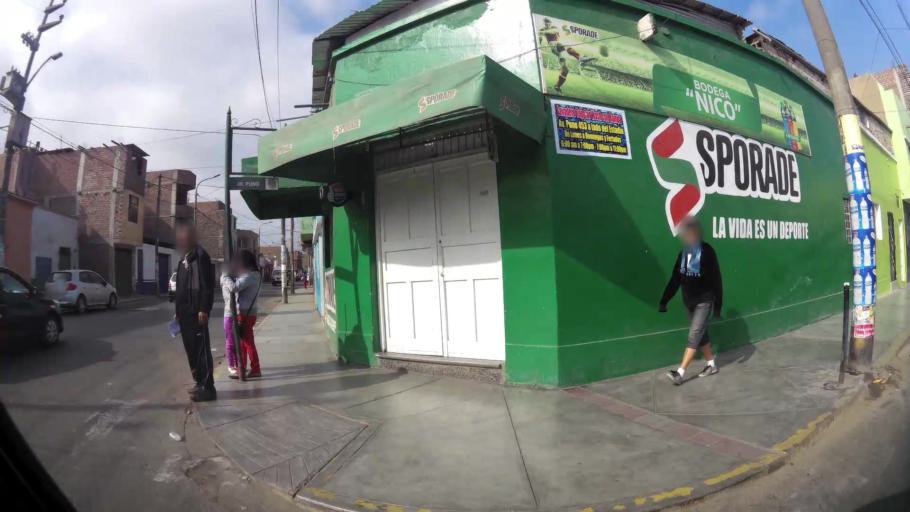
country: PE
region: La Libertad
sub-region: Provincia de Trujillo
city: Trujillo
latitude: -8.1046
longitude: -79.0179
